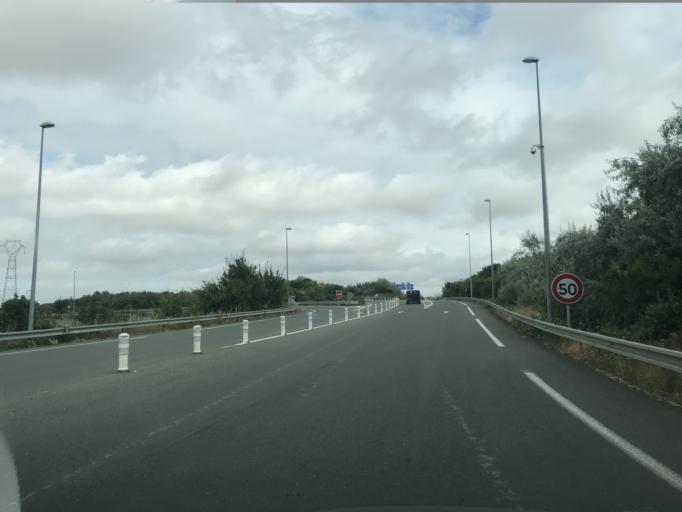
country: FR
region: Poitou-Charentes
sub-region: Departement de la Vienne
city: Jaunay-Clan
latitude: 46.6699
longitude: 0.3597
